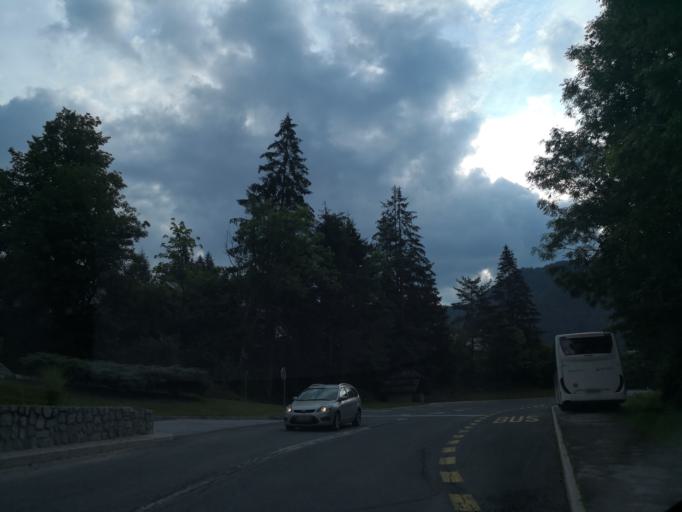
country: SI
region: Jezersko
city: Zgornje Jezersko
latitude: 46.3927
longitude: 14.4948
